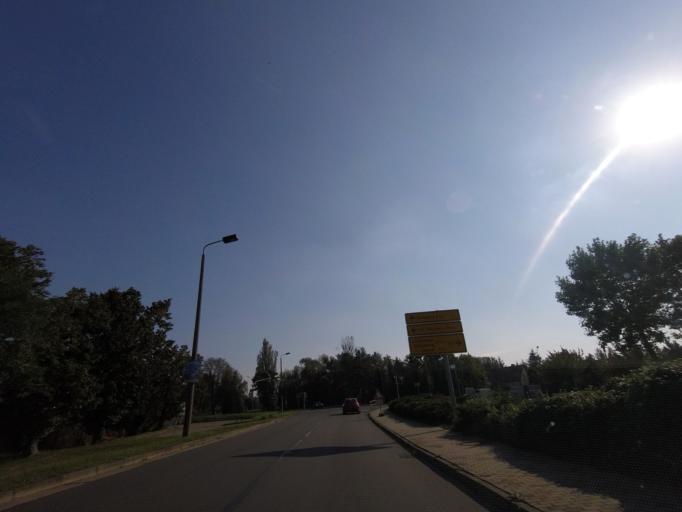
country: DE
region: Saxony-Anhalt
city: Jessen
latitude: 51.7969
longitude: 13.0185
